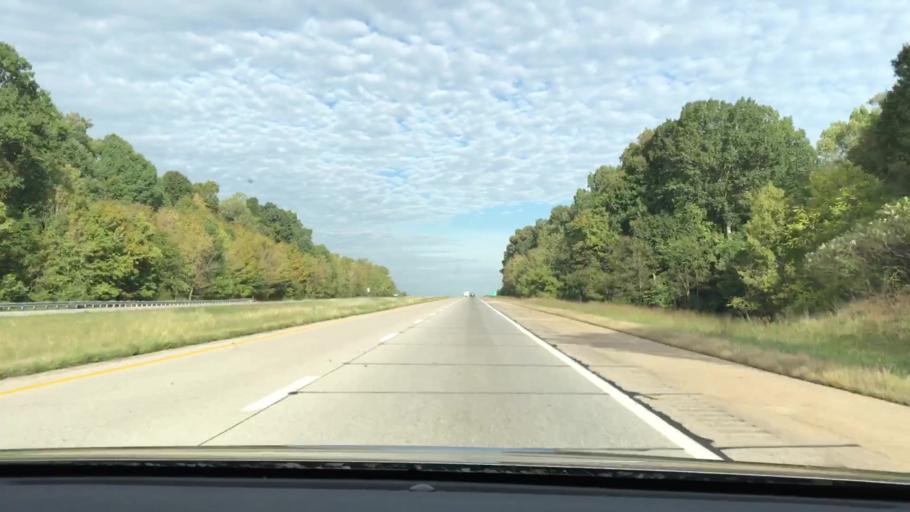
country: US
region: Kentucky
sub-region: Lyon County
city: Eddyville
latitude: 37.0504
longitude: -88.0239
